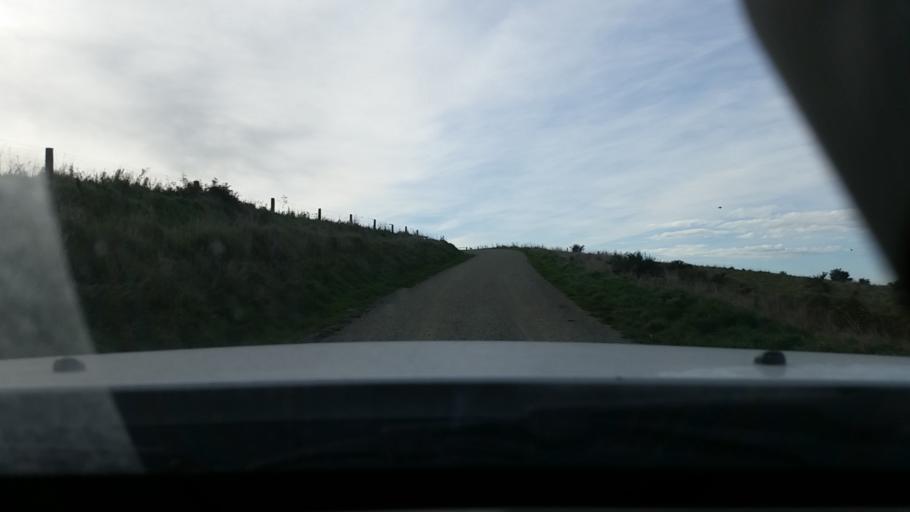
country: NZ
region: Canterbury
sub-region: Timaru District
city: Pleasant Point
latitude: -44.2071
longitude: 171.1818
